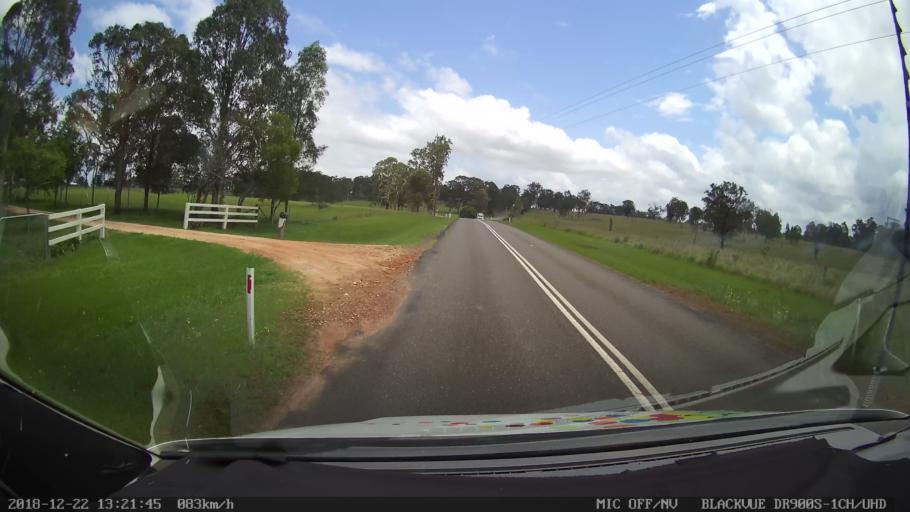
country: AU
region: New South Wales
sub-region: Clarence Valley
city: Coutts Crossing
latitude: -29.7801
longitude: 152.9173
